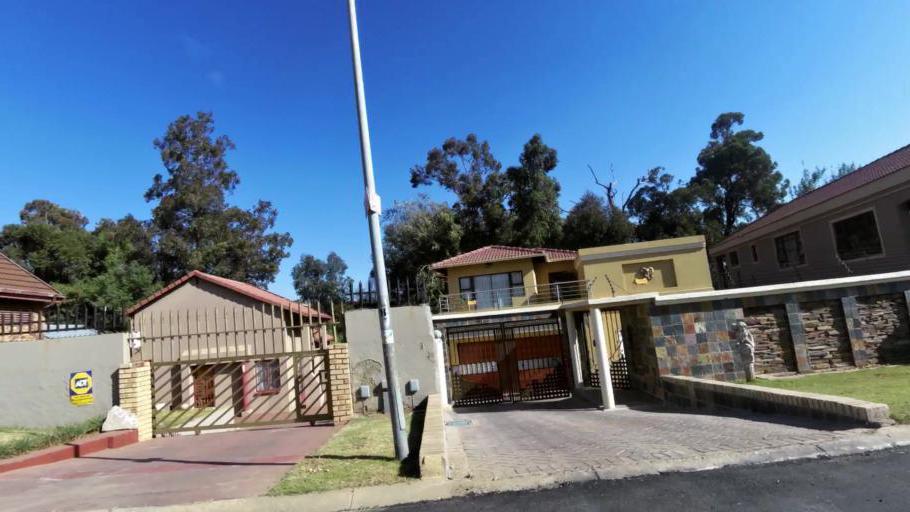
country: ZA
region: Gauteng
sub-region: City of Johannesburg Metropolitan Municipality
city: Johannesburg
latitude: -26.2499
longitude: 27.9903
